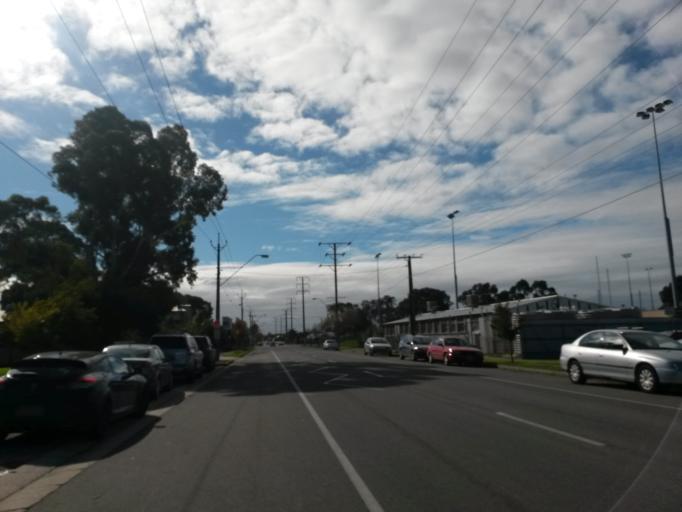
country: AU
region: South Australia
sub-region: Charles Sturt
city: West Lakes Shore
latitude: -34.8469
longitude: 138.4861
